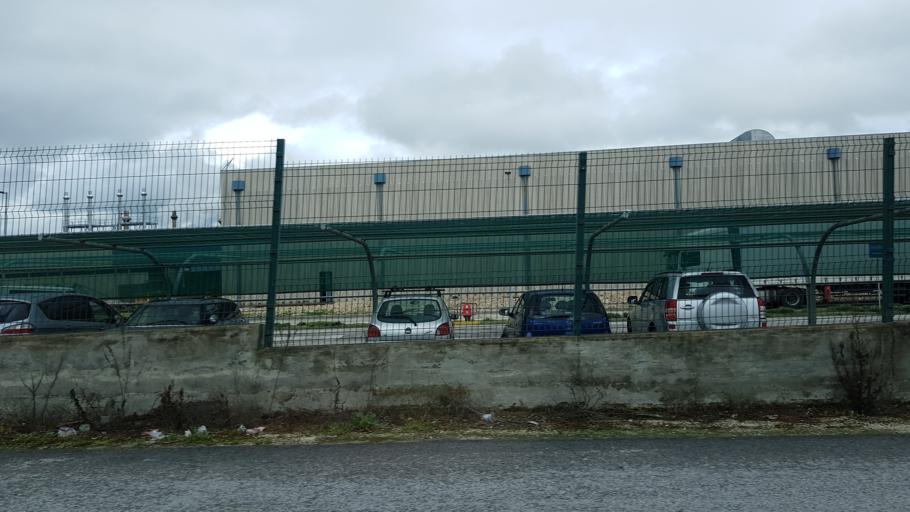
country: PT
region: Lisbon
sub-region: Alenquer
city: Carregado
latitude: 39.0334
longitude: -8.9756
